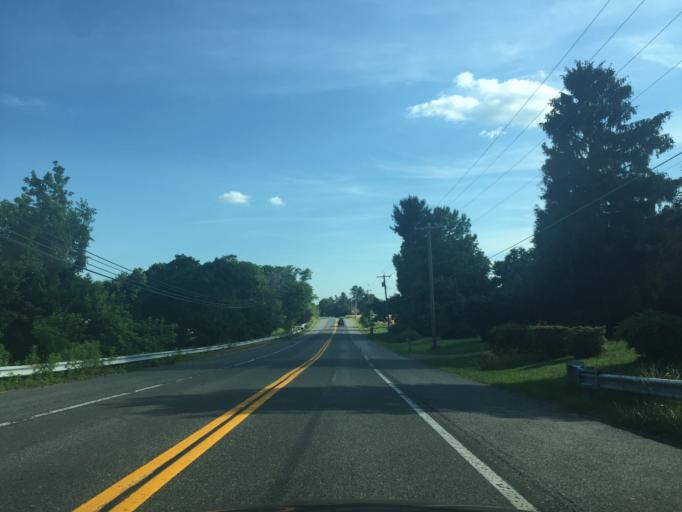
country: US
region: Maryland
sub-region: Harford County
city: Jarrettsville
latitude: 39.6466
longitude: -76.4702
